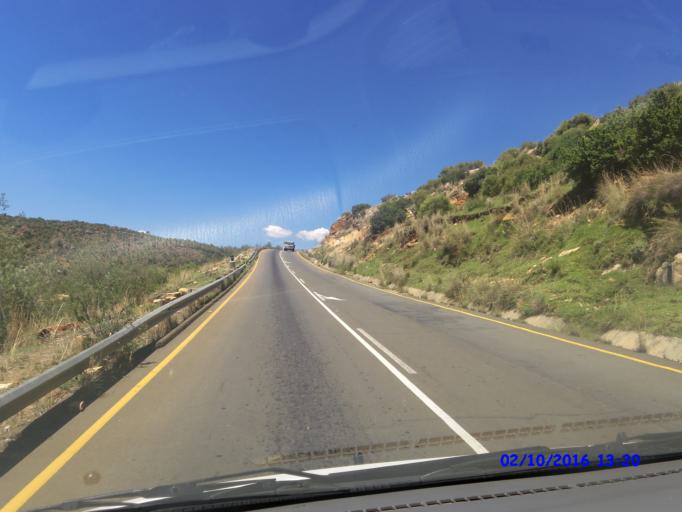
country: LS
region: Maseru
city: Nako
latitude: -29.4214
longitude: 27.7020
